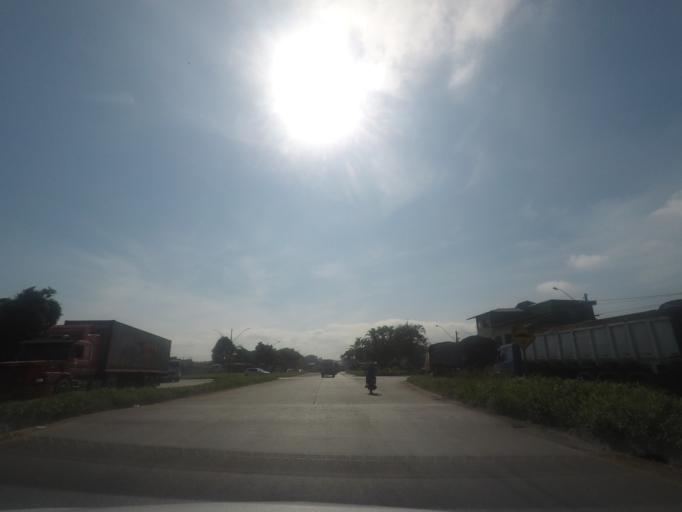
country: BR
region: Parana
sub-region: Paranagua
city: Paranagua
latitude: -25.5156
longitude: -48.5230
